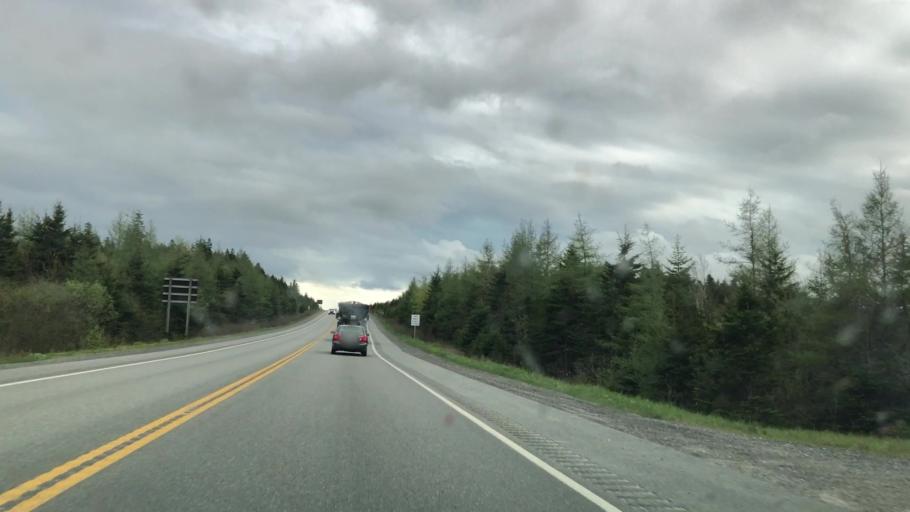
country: CA
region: Nova Scotia
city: Cole Harbour
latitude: 44.7794
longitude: -63.1777
